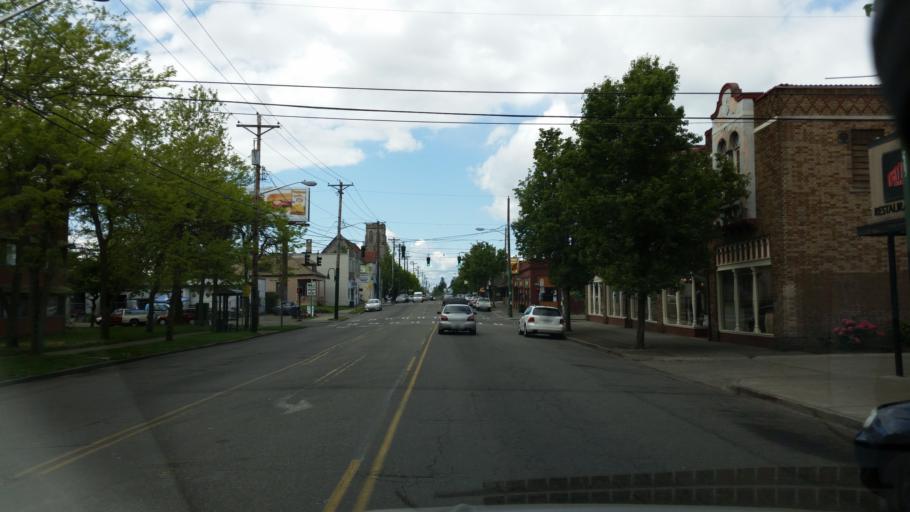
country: US
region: Washington
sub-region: Pierce County
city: Tacoma
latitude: 47.2555
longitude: -122.4674
